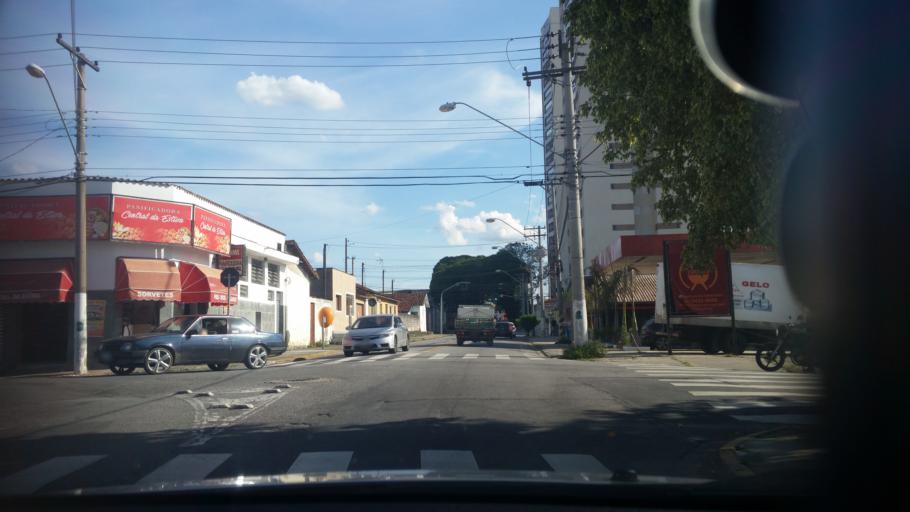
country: BR
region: Sao Paulo
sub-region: Taubate
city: Taubate
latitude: -23.0223
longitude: -45.5712
